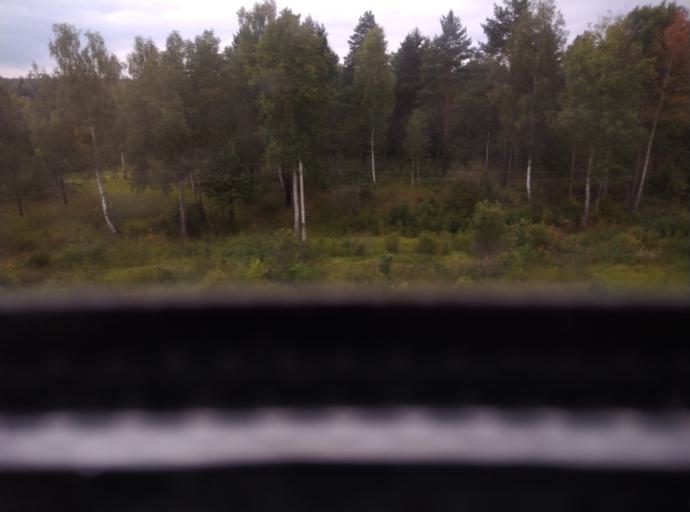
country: RU
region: Kostroma
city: Nerekhta
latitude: 57.4505
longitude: 40.4403
